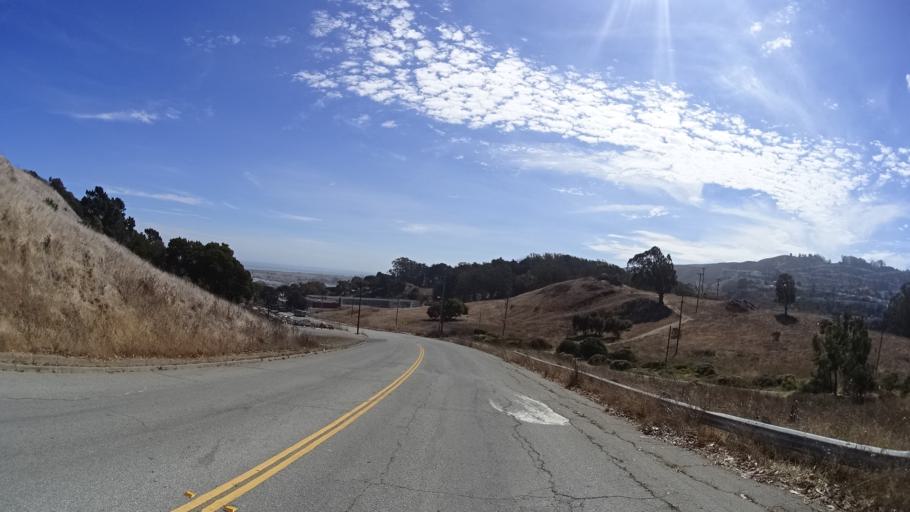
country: US
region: California
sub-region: San Mateo County
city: Daly City
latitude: 37.7154
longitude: -122.4258
